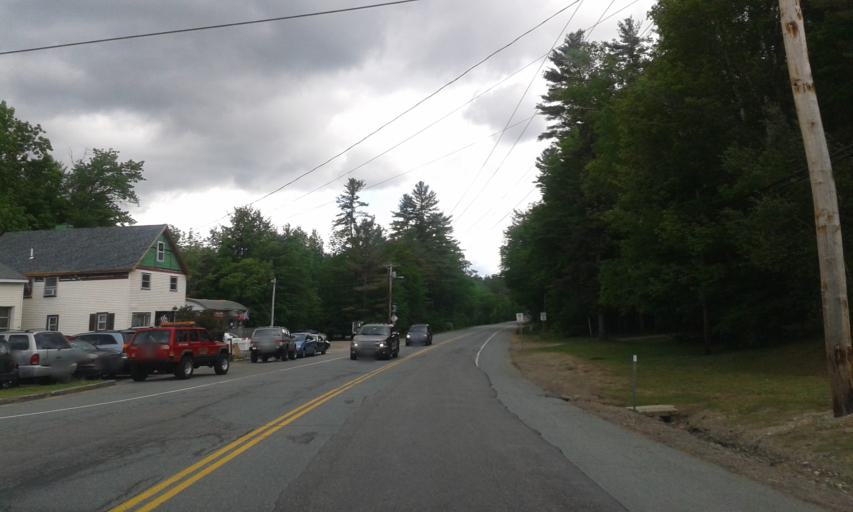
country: US
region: New Hampshire
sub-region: Grafton County
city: Woodstock
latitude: 44.0473
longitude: -71.6863
